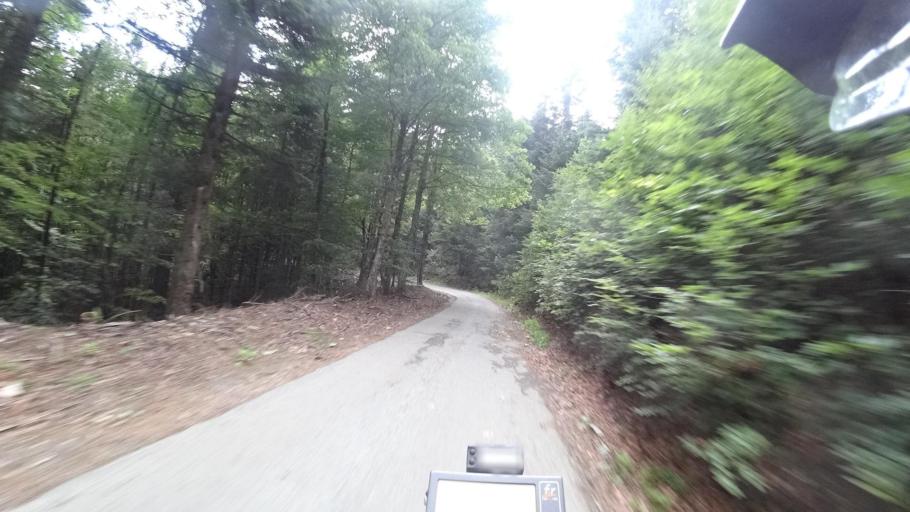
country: HR
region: Licko-Senjska
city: Senj
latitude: 45.1076
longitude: 14.9950
